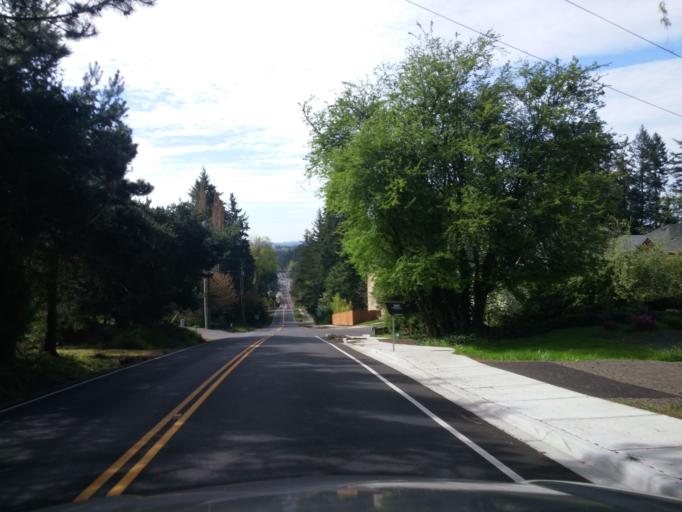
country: US
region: Oregon
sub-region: Washington County
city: Cedar Mill
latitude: 45.5336
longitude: -122.7927
